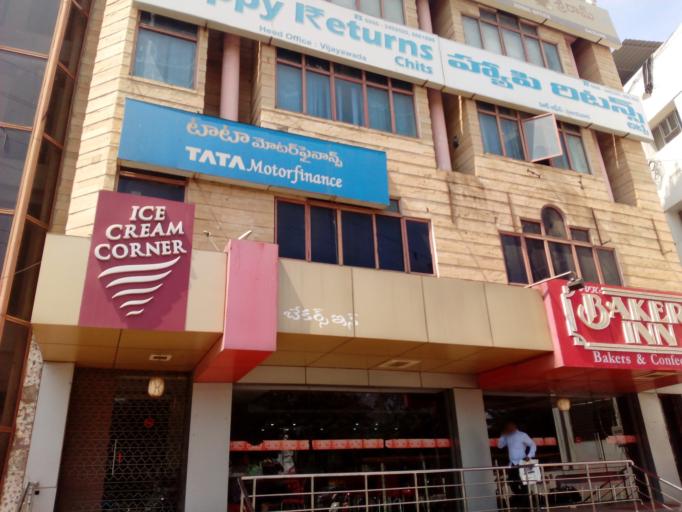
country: IN
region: Andhra Pradesh
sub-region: Krishna
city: Yanamalakuduru
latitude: 16.4994
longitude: 80.6551
